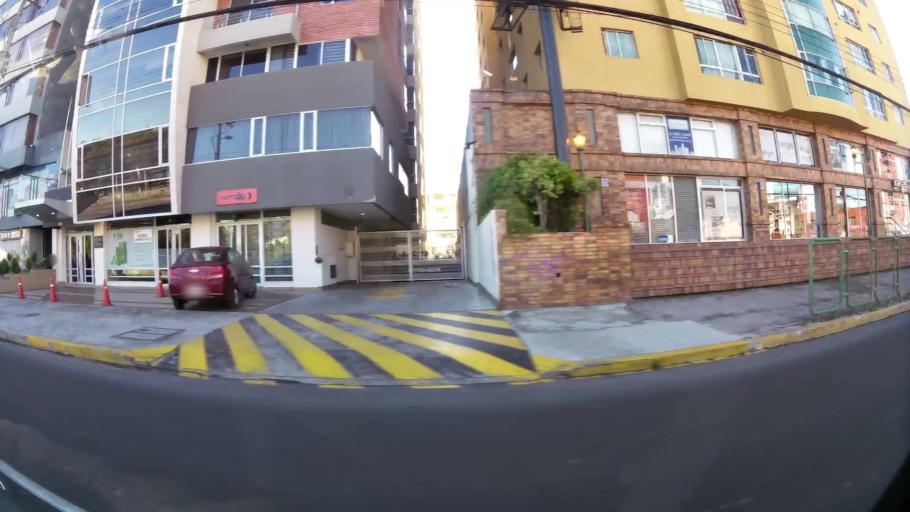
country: EC
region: Pichincha
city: Quito
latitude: -0.1731
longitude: -78.4768
